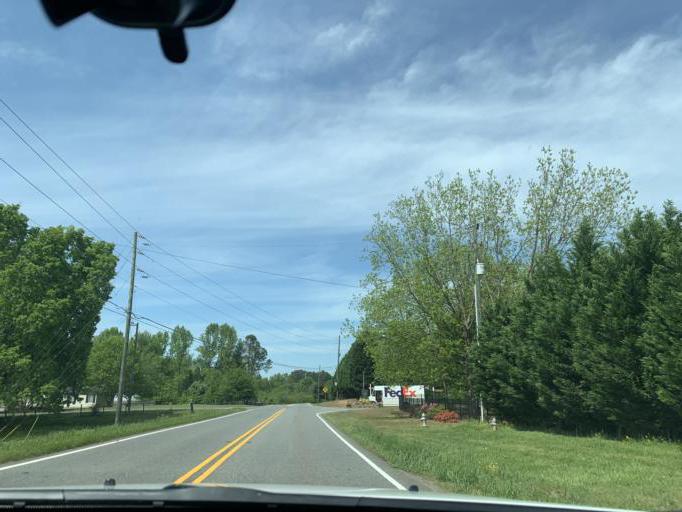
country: US
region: Georgia
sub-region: Forsyth County
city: Cumming
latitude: 34.2567
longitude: -84.1707
